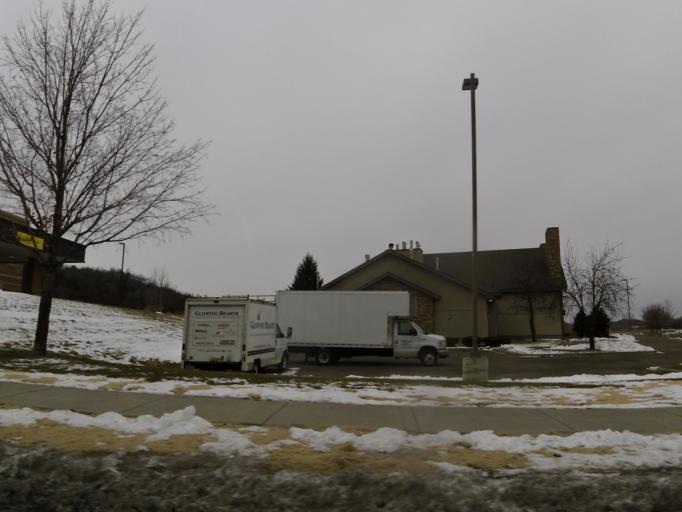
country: US
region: Minnesota
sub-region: Scott County
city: Jordan
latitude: 44.6674
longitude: -93.6358
